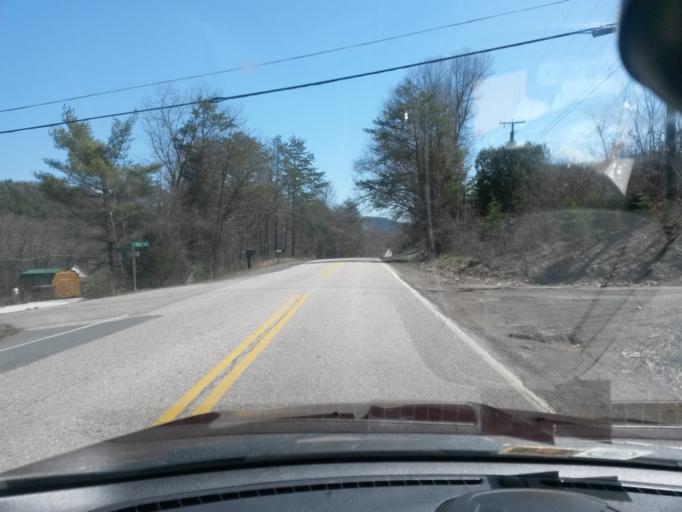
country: US
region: Virginia
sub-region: City of Covington
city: Covington
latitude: 37.8171
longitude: -80.1122
